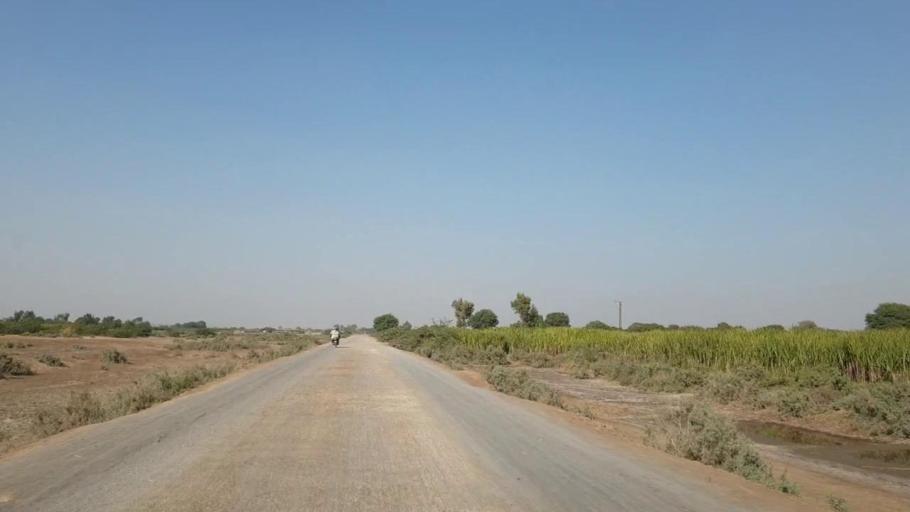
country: PK
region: Sindh
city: Digri
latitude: 25.0389
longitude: 69.1048
